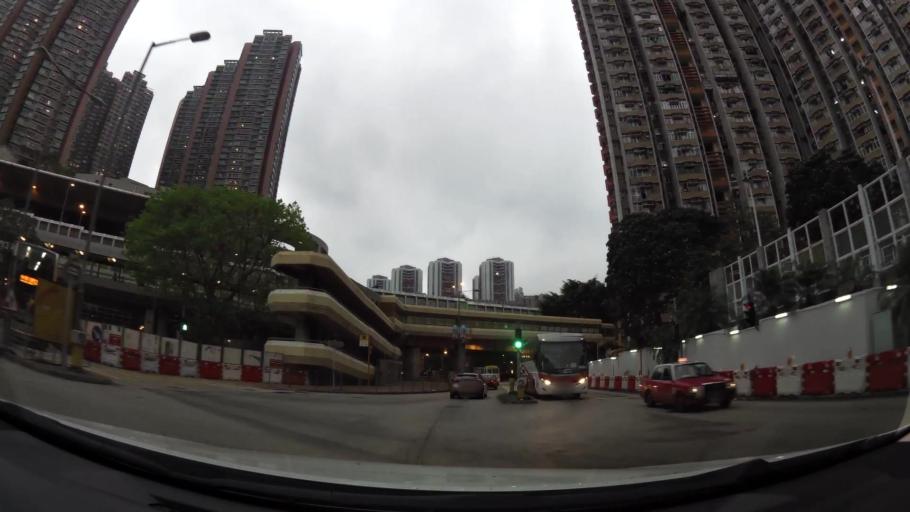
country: HK
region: Tsuen Wan
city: Tsuen Wan
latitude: 22.3600
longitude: 114.1059
